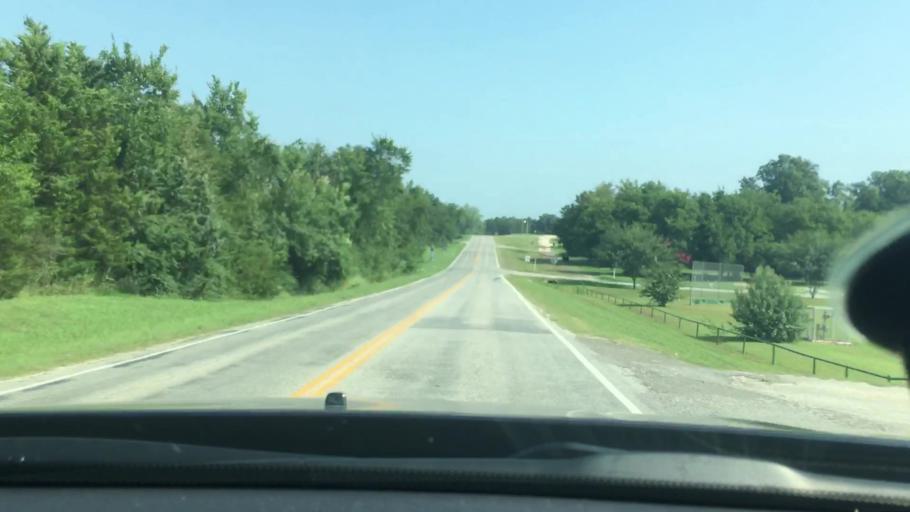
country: US
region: Oklahoma
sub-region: Pontotoc County
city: Ada
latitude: 34.6476
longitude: -96.5298
